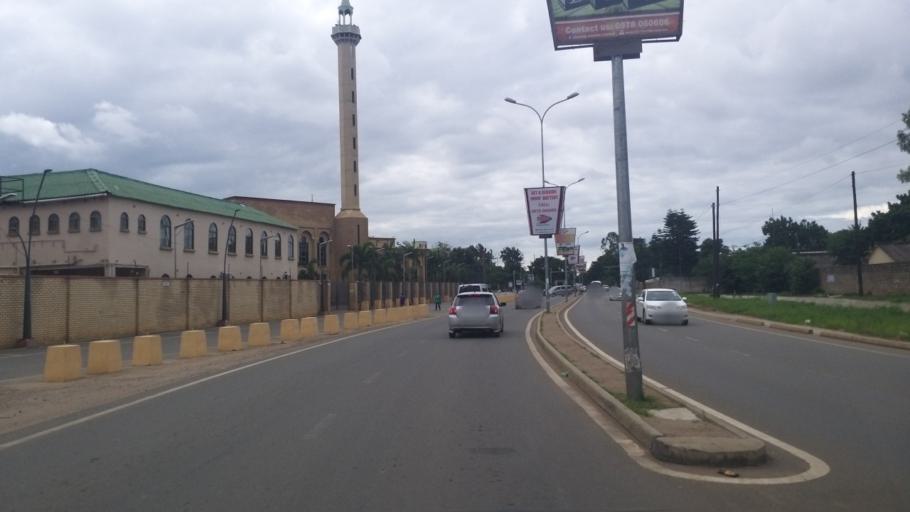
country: ZM
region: Lusaka
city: Lusaka
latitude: -15.4242
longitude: 28.2949
